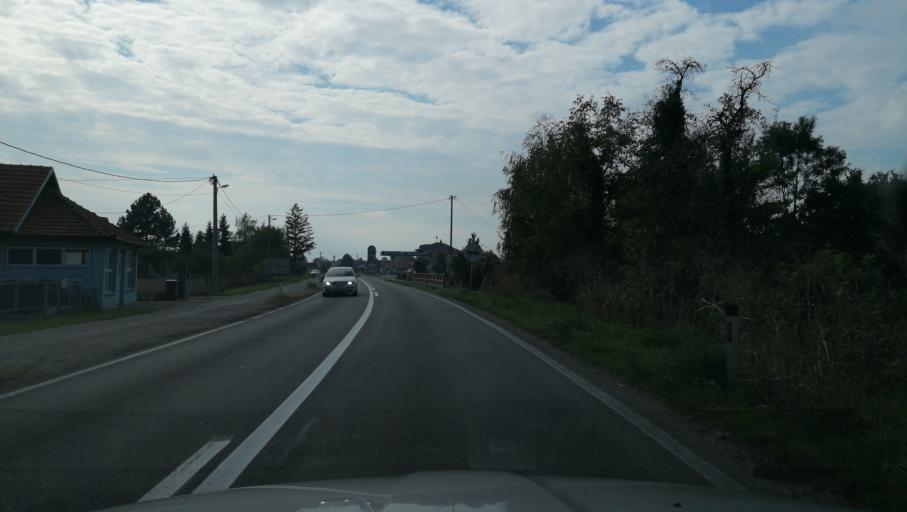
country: BA
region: Republika Srpska
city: Dvorovi
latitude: 44.8159
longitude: 19.2706
